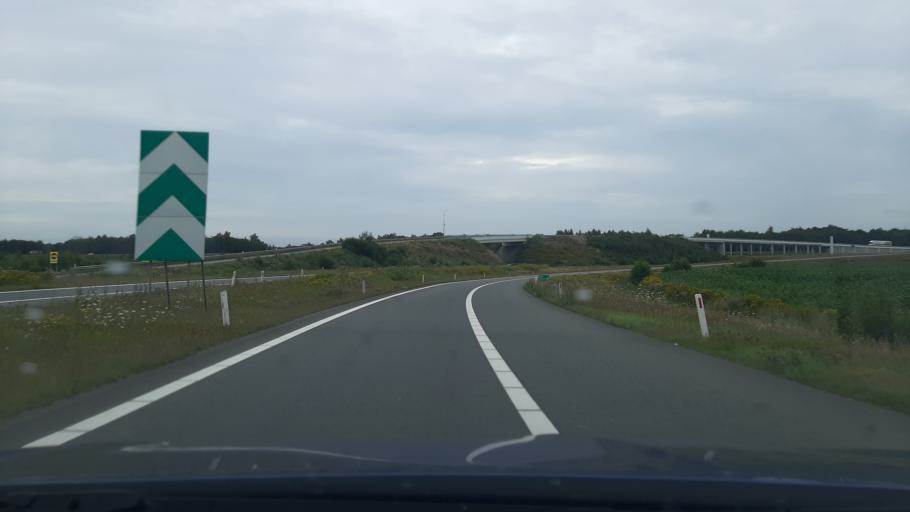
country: NL
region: Drenthe
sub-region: Gemeente Assen
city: Assen
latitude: 52.9679
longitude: 6.5478
